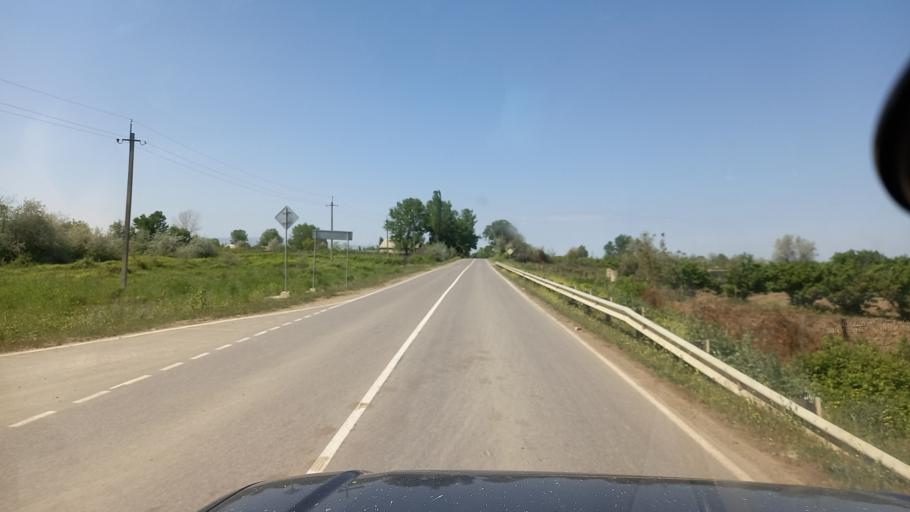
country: RU
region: Dagestan
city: Novaya Maka
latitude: 41.8116
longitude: 48.4051
